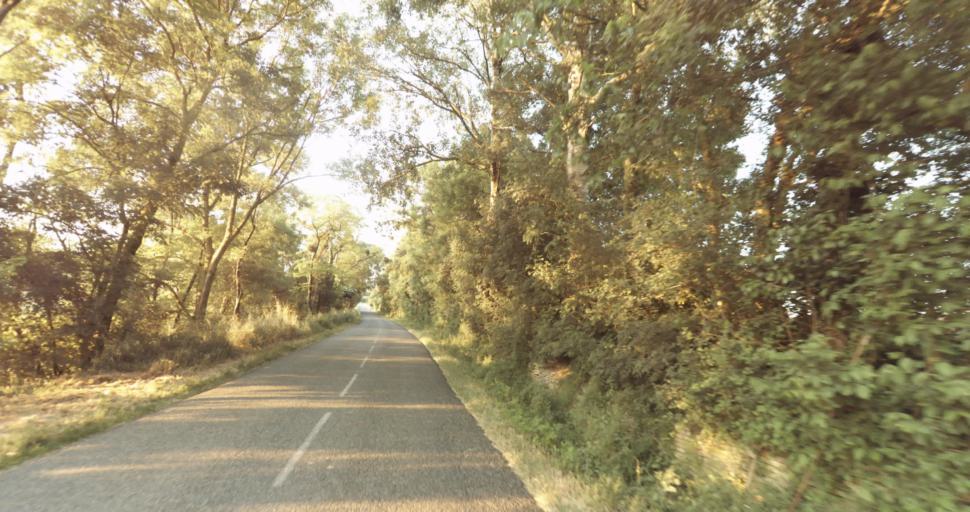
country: FR
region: Midi-Pyrenees
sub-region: Departement du Gers
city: Pujaudran
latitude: 43.6163
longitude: 1.1569
